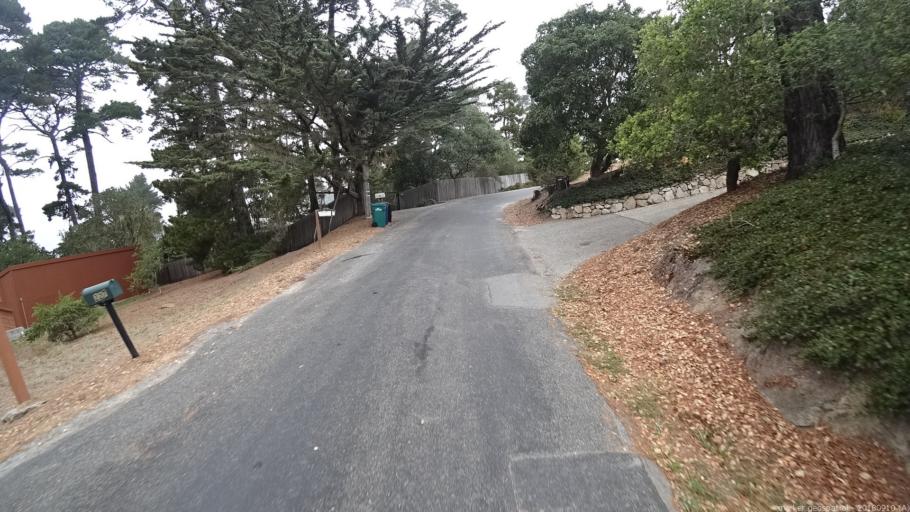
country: US
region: California
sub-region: Monterey County
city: Carmel-by-the-Sea
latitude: 36.4958
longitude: -121.9355
